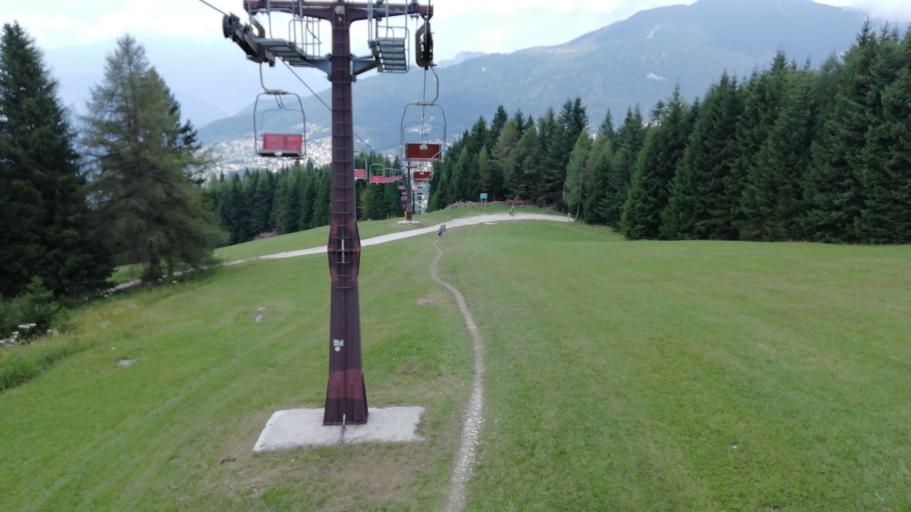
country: IT
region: Trentino-Alto Adige
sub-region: Provincia di Trento
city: Folgaria
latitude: 45.8966
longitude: 11.1941
